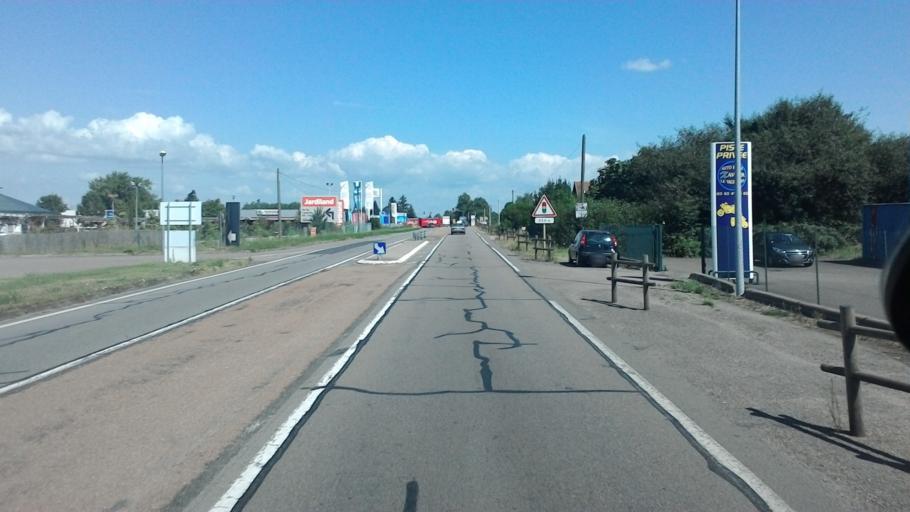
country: FR
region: Bourgogne
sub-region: Departement de Saone-et-Loire
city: Sevrey
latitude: 46.7461
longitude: 4.8515
